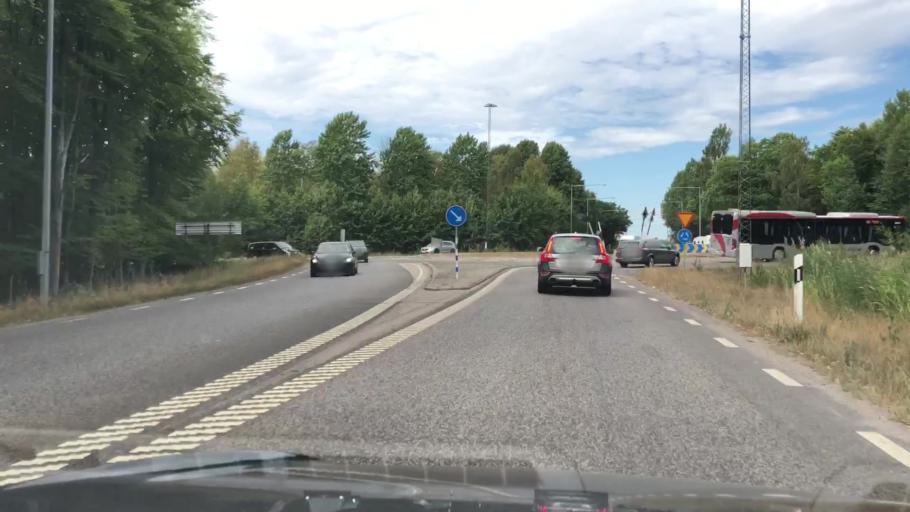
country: SE
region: Blekinge
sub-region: Karlskrona Kommun
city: Jaemjoe
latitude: 56.1843
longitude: 15.7210
